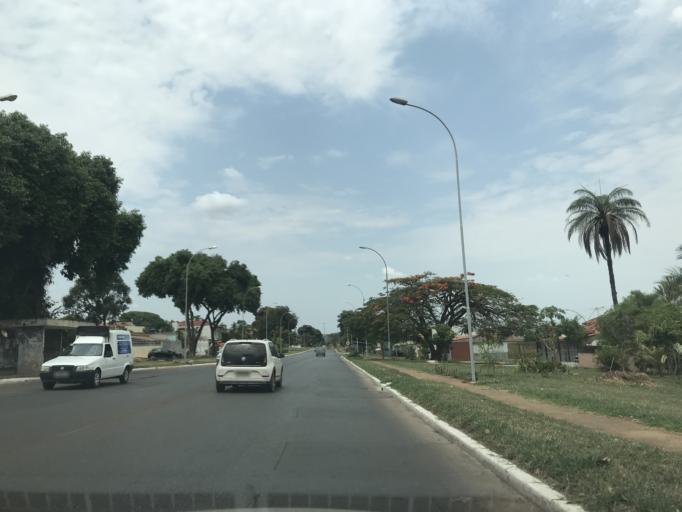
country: BR
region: Federal District
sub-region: Brasilia
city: Brasilia
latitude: -15.6490
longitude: -47.8036
